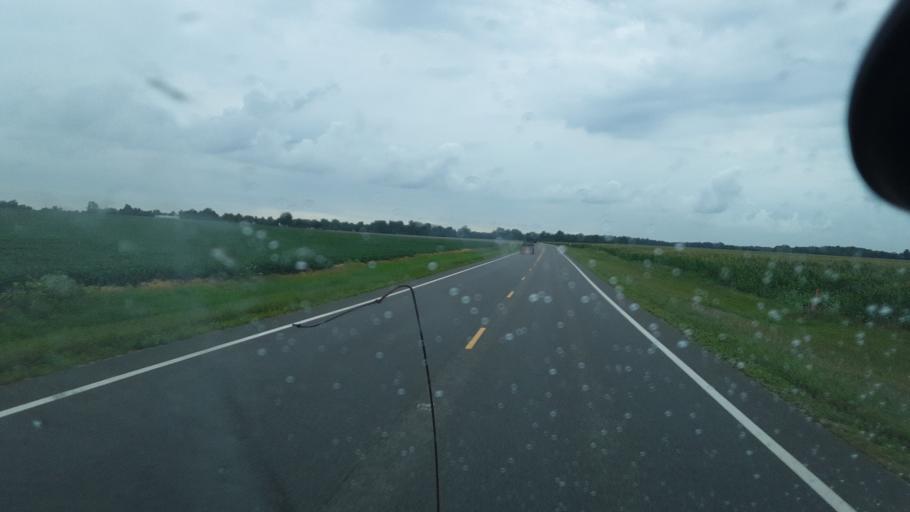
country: US
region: Ohio
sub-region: Williams County
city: Bryan
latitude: 41.4175
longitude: -84.6174
